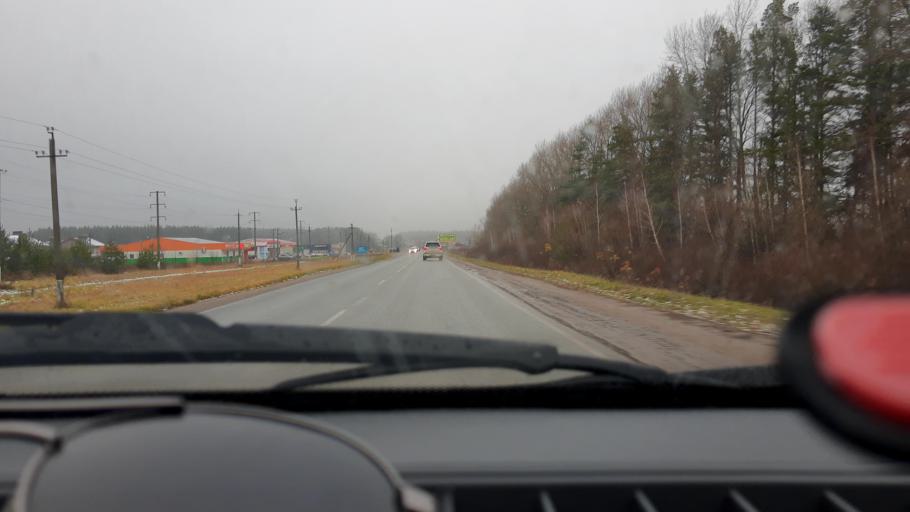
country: RU
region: Bashkortostan
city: Kabakovo
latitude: 54.6099
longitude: 56.1741
